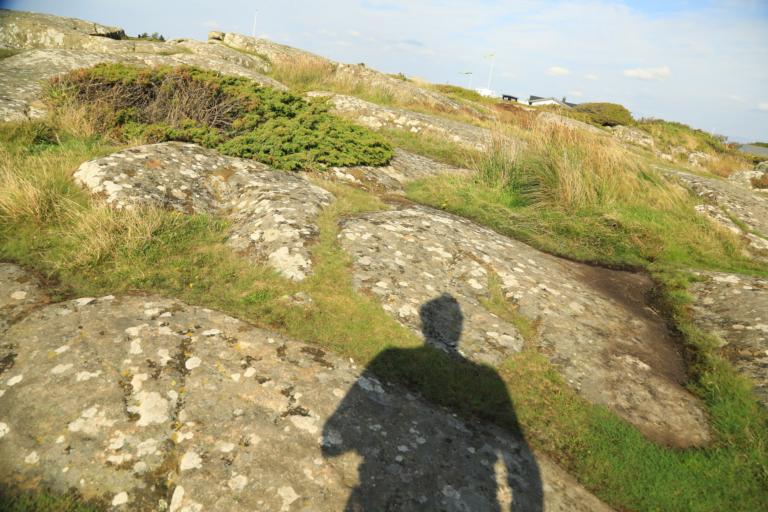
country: SE
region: Halland
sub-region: Varbergs Kommun
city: Varberg
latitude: 57.1150
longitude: 12.2102
